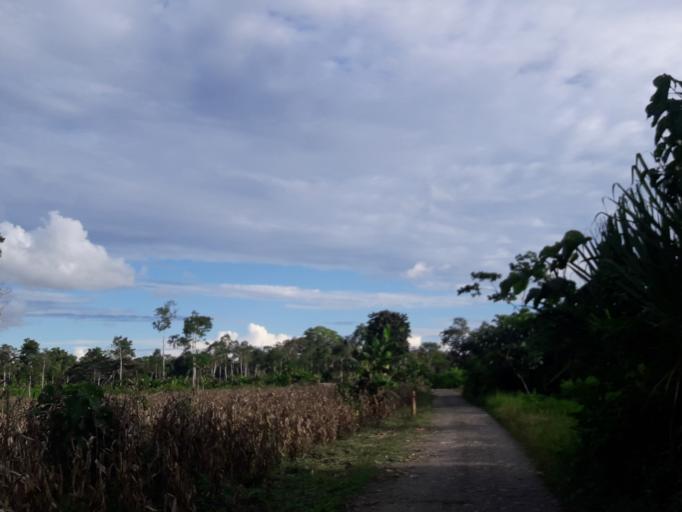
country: EC
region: Orellana
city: Boca Suno
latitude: -0.8931
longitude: -77.3076
